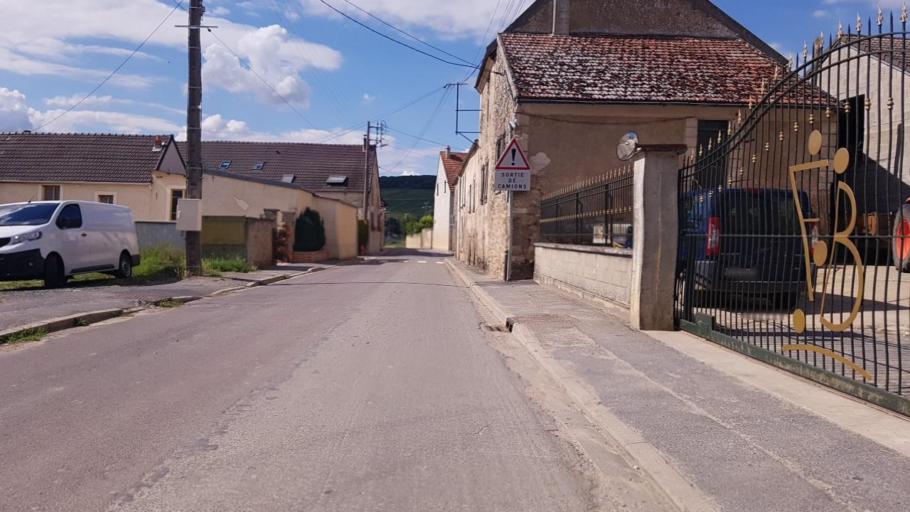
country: FR
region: Picardie
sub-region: Departement de l'Aisne
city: Crezancy
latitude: 49.0742
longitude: 3.5625
